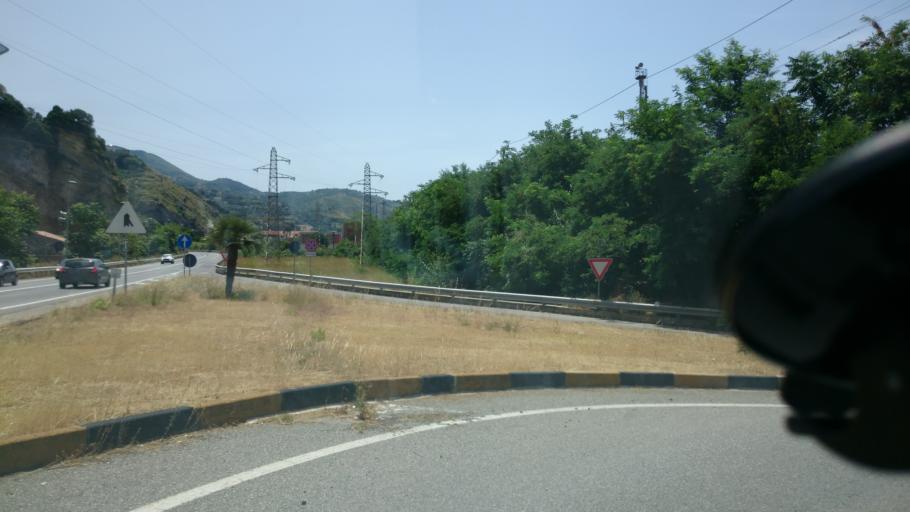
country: IT
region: Calabria
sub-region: Provincia di Cosenza
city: Cetraro Marina
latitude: 39.5167
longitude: 15.9357
